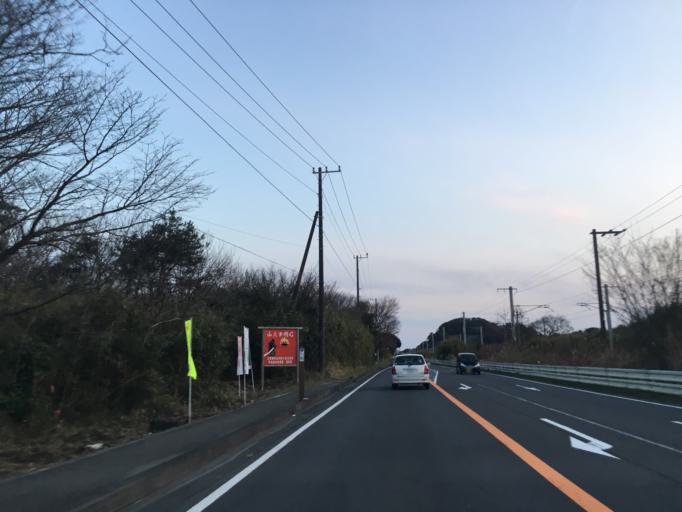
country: JP
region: Ibaraki
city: Kitaibaraki
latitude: 36.7707
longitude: 140.7390
